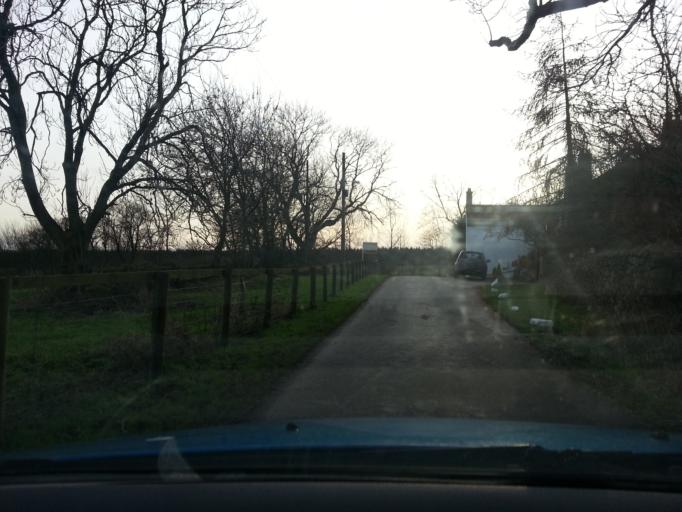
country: GB
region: England
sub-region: County Durham
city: Tow Law
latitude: 54.7302
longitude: -1.7699
